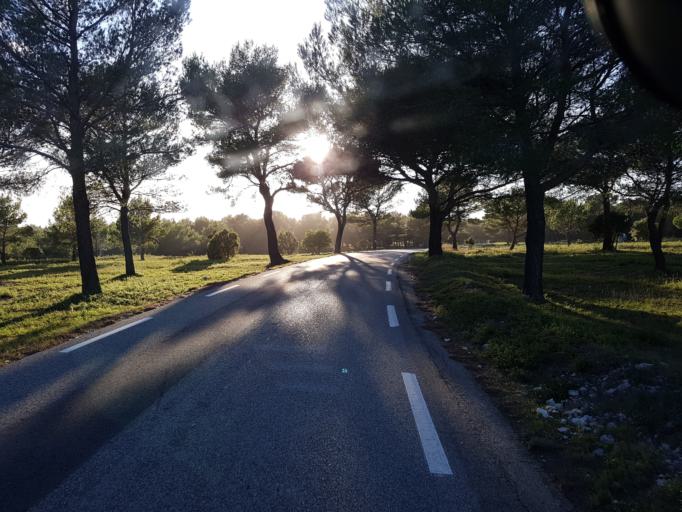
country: FR
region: Provence-Alpes-Cote d'Azur
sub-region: Departement des Bouches-du-Rhone
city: Cuges-les-Pins
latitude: 43.2472
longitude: 5.7253
